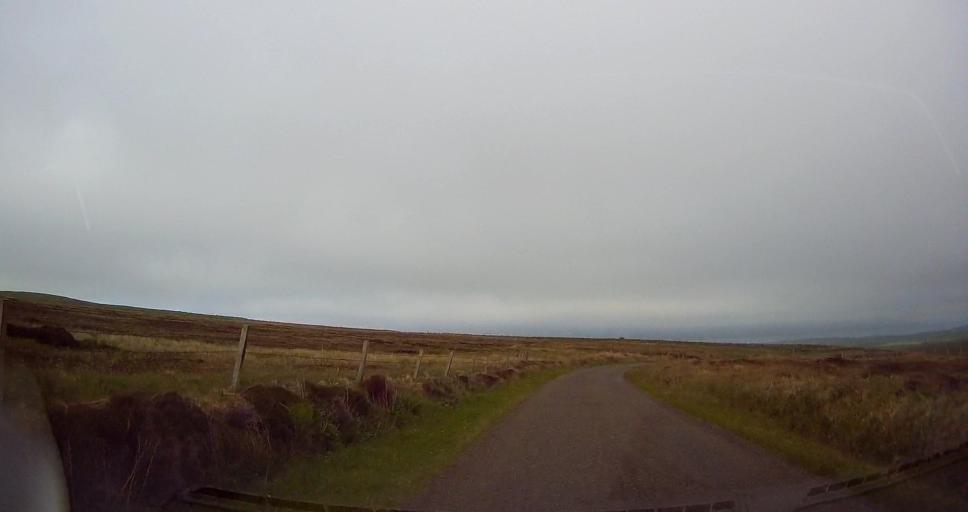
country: GB
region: Scotland
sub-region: Orkney Islands
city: Orkney
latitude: 59.1036
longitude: -3.1345
